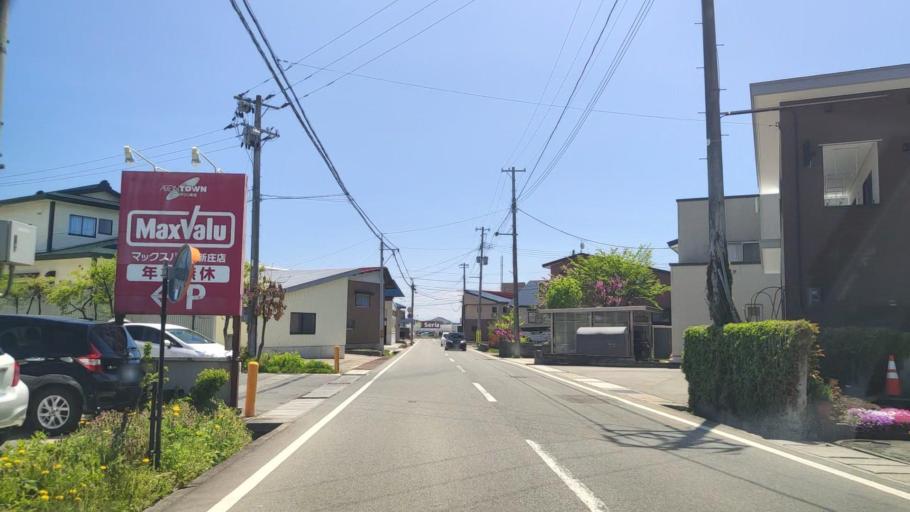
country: JP
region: Yamagata
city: Shinjo
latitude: 38.7725
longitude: 140.3076
